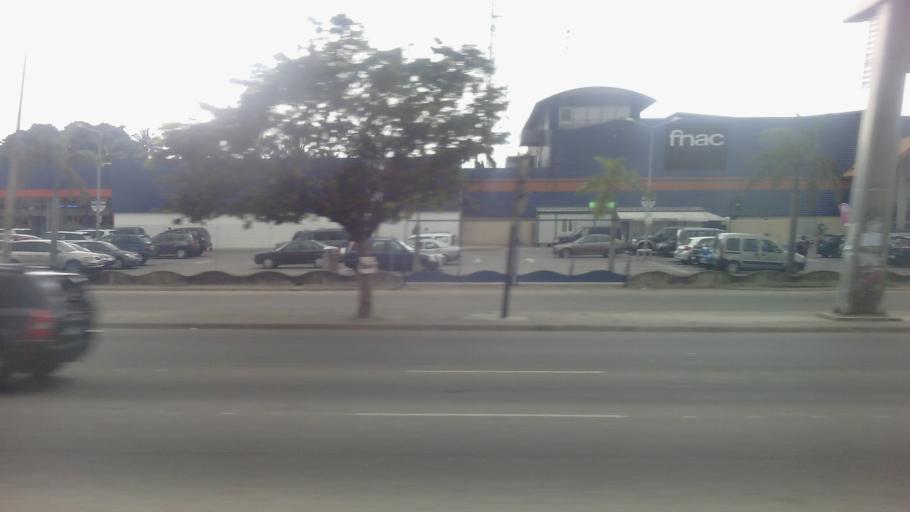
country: CI
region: Lagunes
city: Abidjan
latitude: 5.2986
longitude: -3.9860
